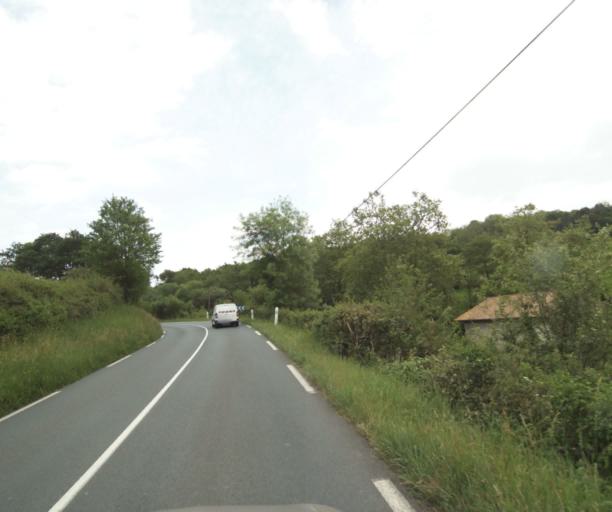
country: FR
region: Aquitaine
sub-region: Departement des Pyrenees-Atlantiques
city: Mouguerre
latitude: 43.4629
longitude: -1.4180
